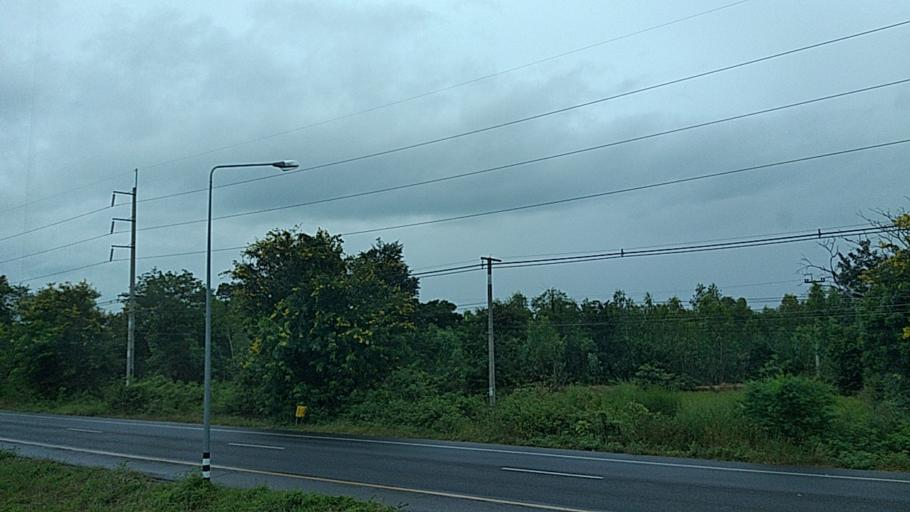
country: TH
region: Maha Sarakham
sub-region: Amphoe Borabue
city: Borabue
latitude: 16.0692
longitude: 103.1474
